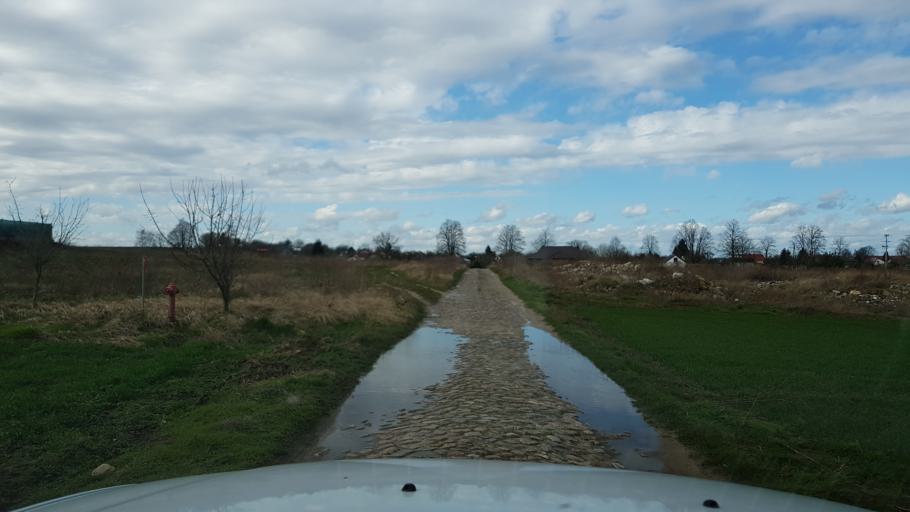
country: PL
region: West Pomeranian Voivodeship
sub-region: Powiat mysliborski
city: Barlinek
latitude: 52.9767
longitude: 15.1760
